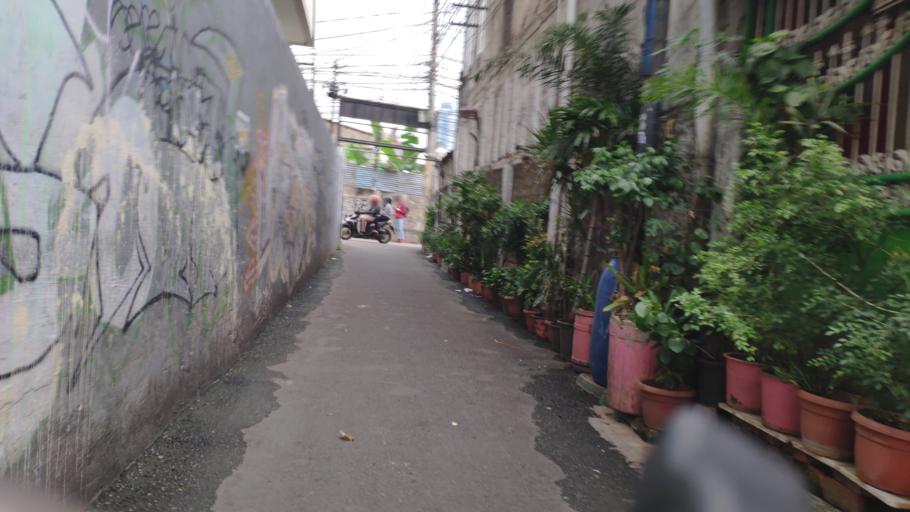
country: ID
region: Jakarta Raya
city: Jakarta
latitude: -6.2119
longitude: 106.8382
